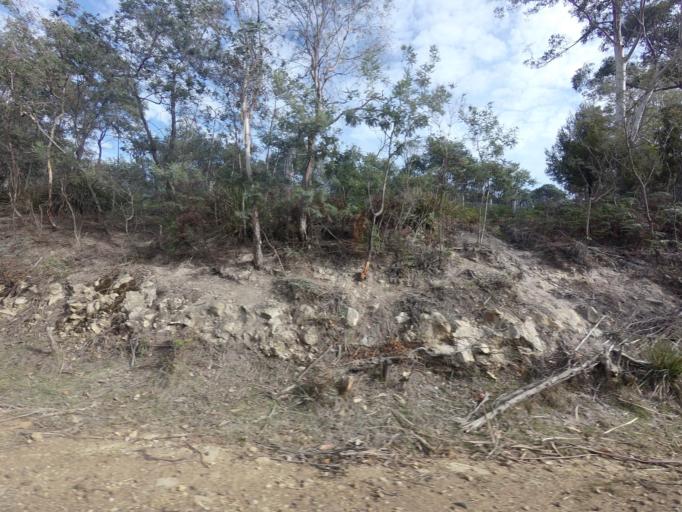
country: AU
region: Tasmania
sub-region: Sorell
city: Sorell
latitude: -42.5630
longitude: 147.4672
